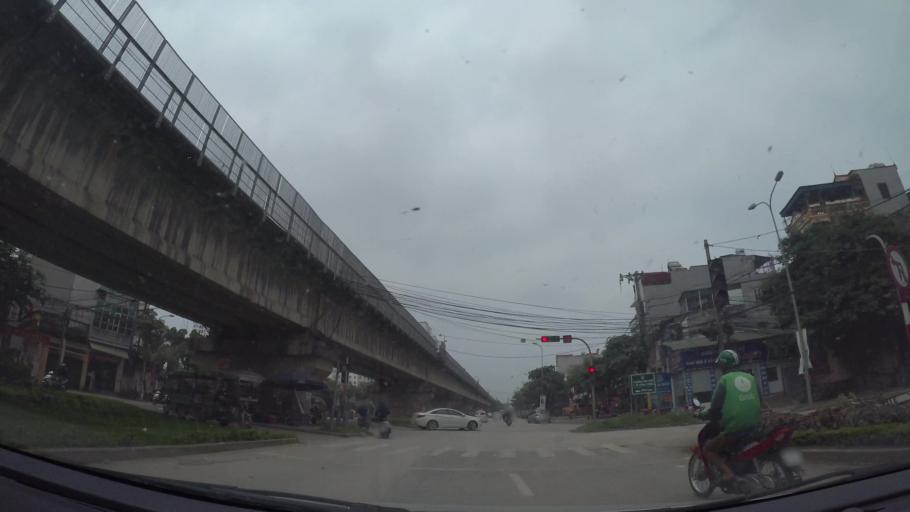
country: VN
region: Ha Noi
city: Tay Ho
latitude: 21.0808
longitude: 105.7856
